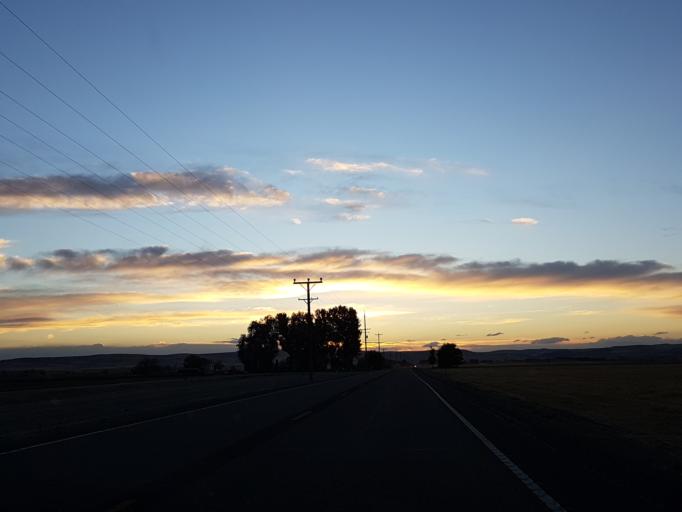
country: US
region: Oregon
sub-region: Malheur County
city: Vale
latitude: 43.9391
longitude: -117.3415
